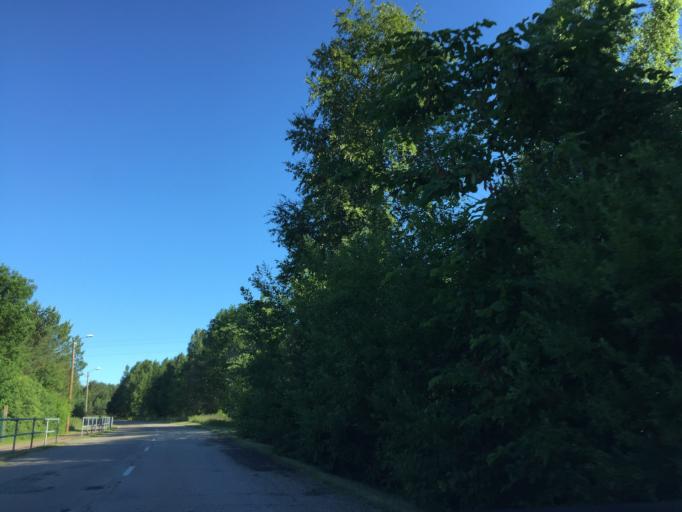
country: LV
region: Ventspils
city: Ventspils
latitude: 57.4371
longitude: 21.6225
